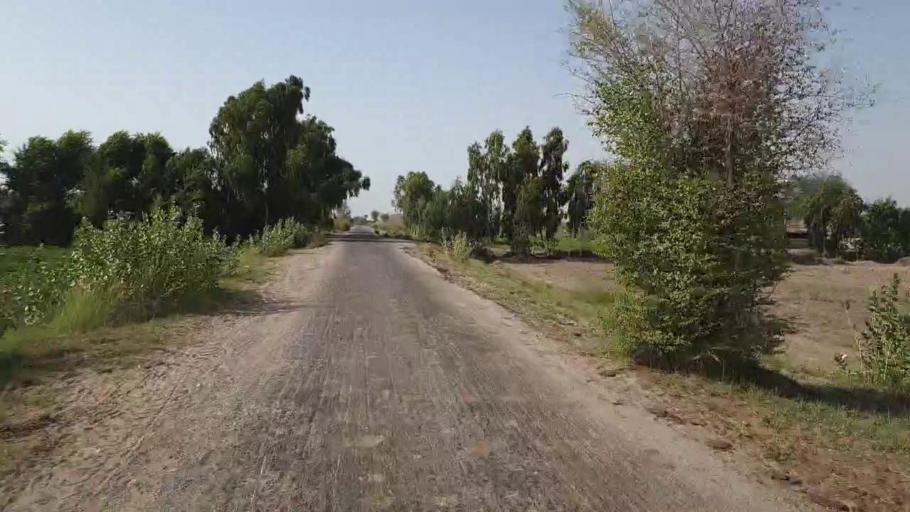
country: PK
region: Sindh
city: Kandiari
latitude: 26.6984
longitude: 68.9646
